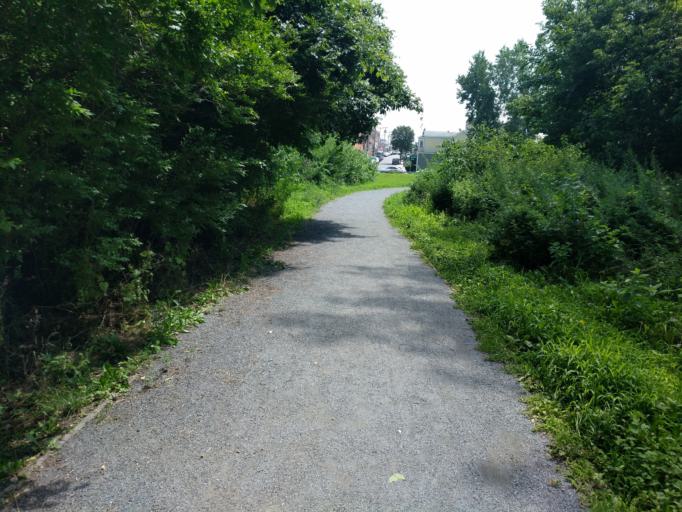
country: US
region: New York
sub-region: Bronx
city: The Bronx
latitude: 40.7887
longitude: -73.8374
